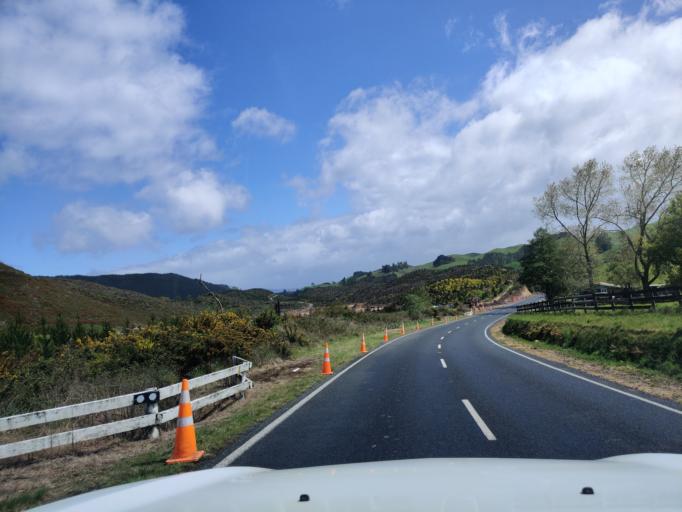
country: NZ
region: Bay of Plenty
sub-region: Rotorua District
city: Rotorua
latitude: -38.1738
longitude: 176.3229
